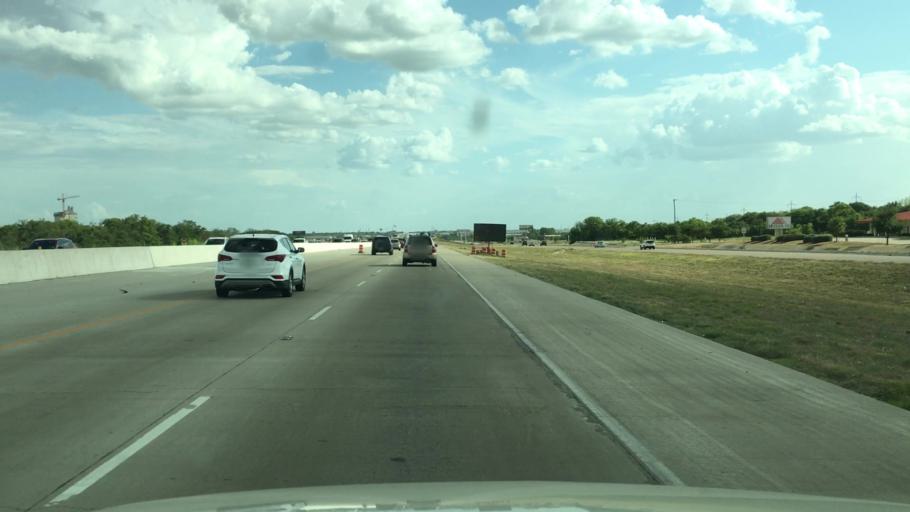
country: US
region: Texas
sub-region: Bell County
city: Troy
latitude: 31.1637
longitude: -97.3208
